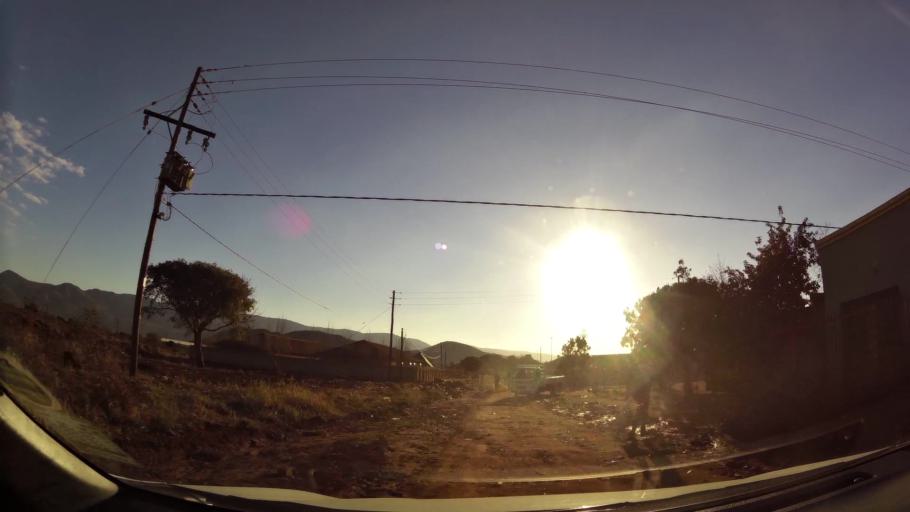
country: ZA
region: Limpopo
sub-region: Waterberg District Municipality
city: Mokopane
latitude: -24.1559
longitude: 28.9924
